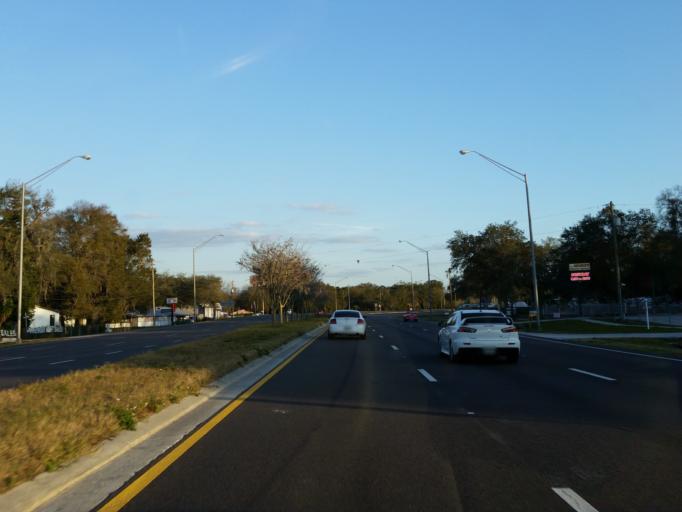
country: US
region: Florida
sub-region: Hillsborough County
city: Riverview
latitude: 27.8856
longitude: -82.3291
